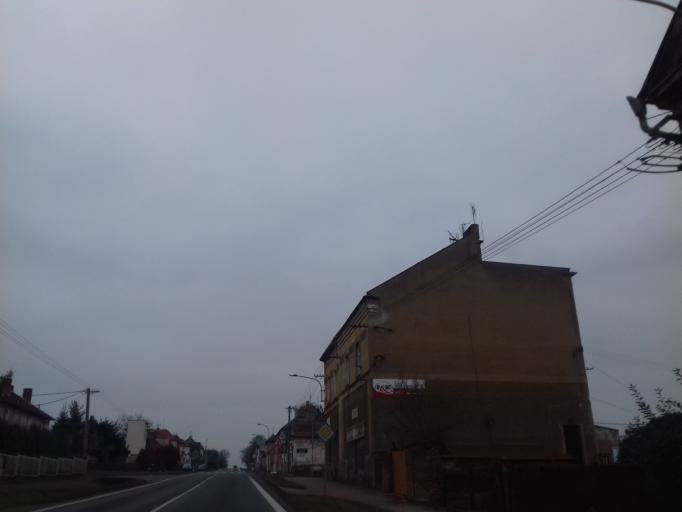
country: CZ
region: Plzensky
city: Zbuch
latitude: 49.6790
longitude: 13.2266
